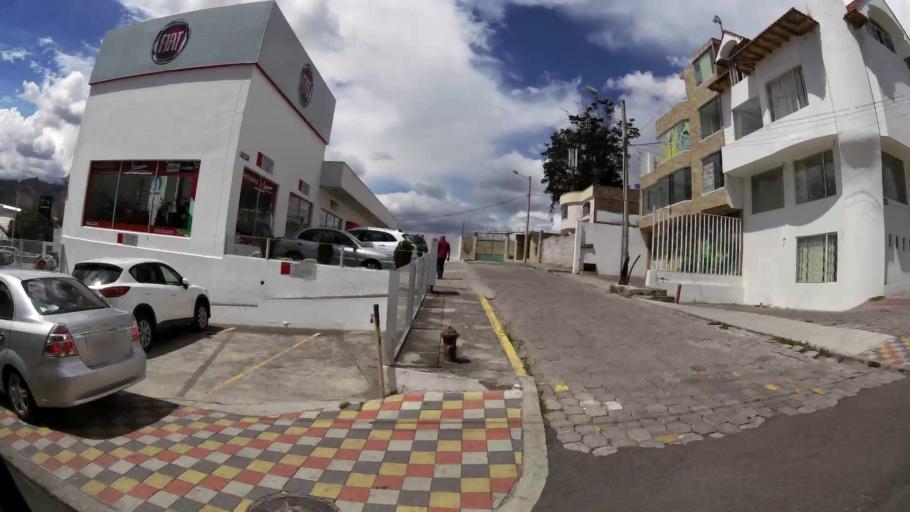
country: EC
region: Tungurahua
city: Ambato
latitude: -1.2643
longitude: -78.6273
